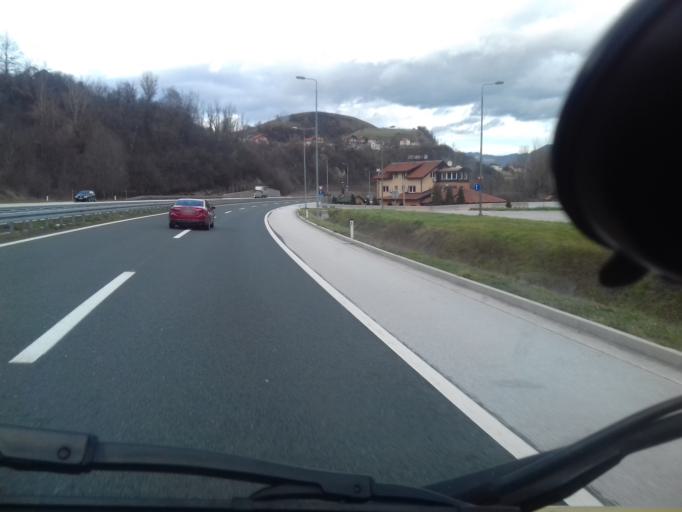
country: BA
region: Federation of Bosnia and Herzegovina
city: Kakanj
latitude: 44.0977
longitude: 18.1069
